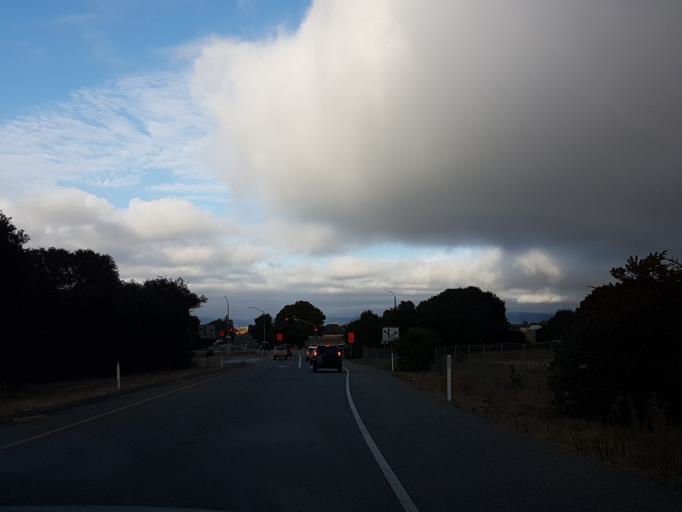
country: US
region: California
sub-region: Monterey County
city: Salinas
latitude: 36.6237
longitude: -121.6827
